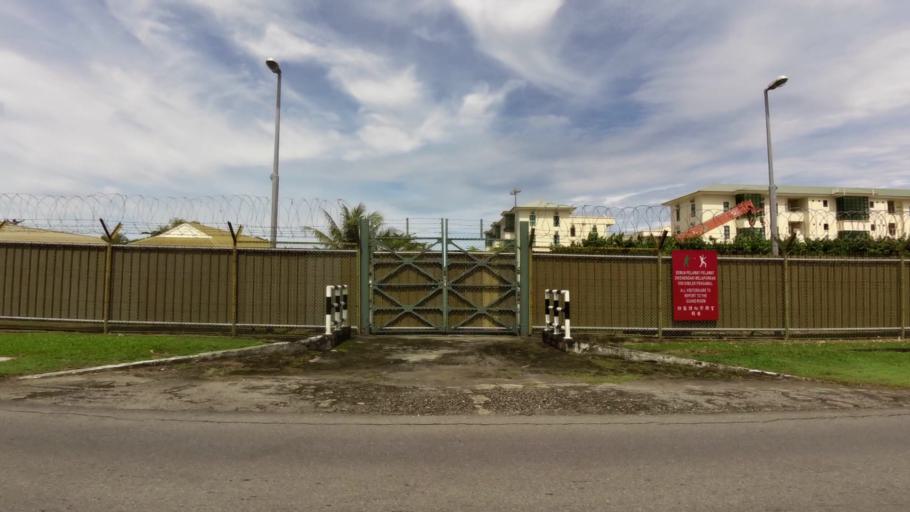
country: BN
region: Belait
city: Seria
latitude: 4.6079
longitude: 114.3160
